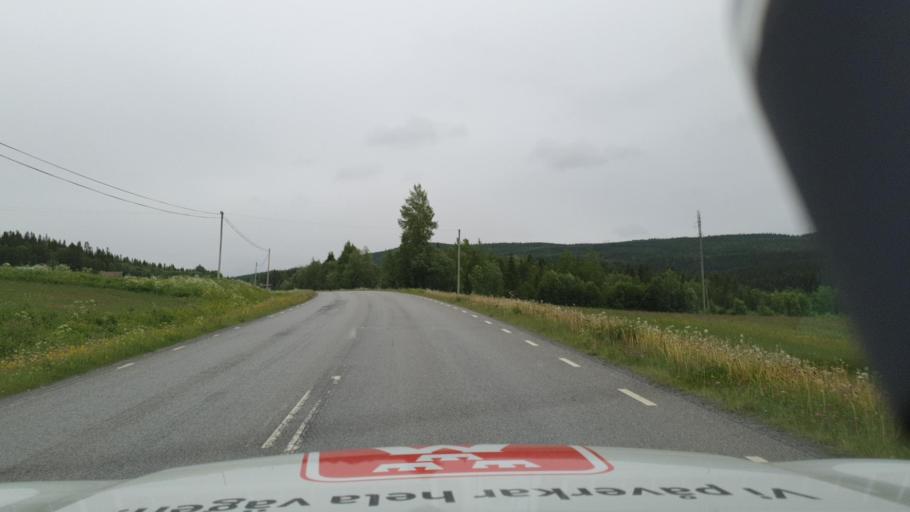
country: SE
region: Jaemtland
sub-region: Are Kommun
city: Jarpen
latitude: 63.4005
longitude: 13.3722
